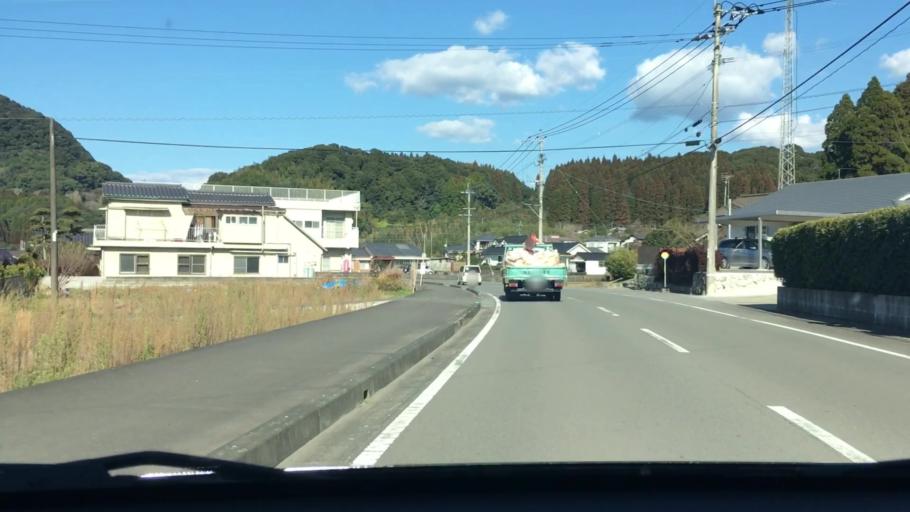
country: JP
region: Kagoshima
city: Satsumasendai
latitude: 31.7924
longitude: 130.4099
